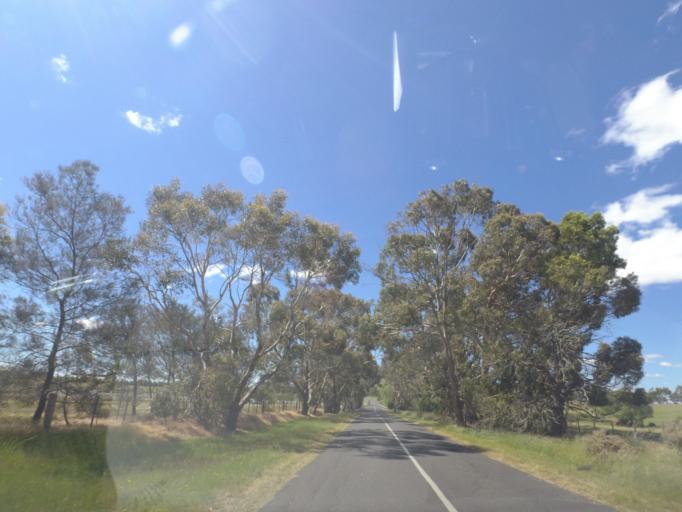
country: AU
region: Victoria
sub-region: Moorabool
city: Bacchus Marsh
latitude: -37.3315
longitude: 144.4430
